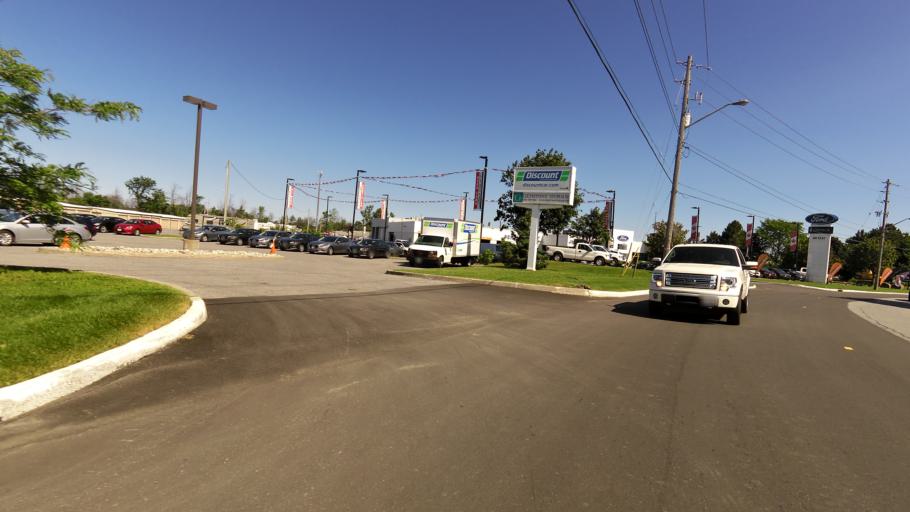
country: CA
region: Quebec
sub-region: Outaouais
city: Gatineau
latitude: 45.4641
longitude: -75.5505
